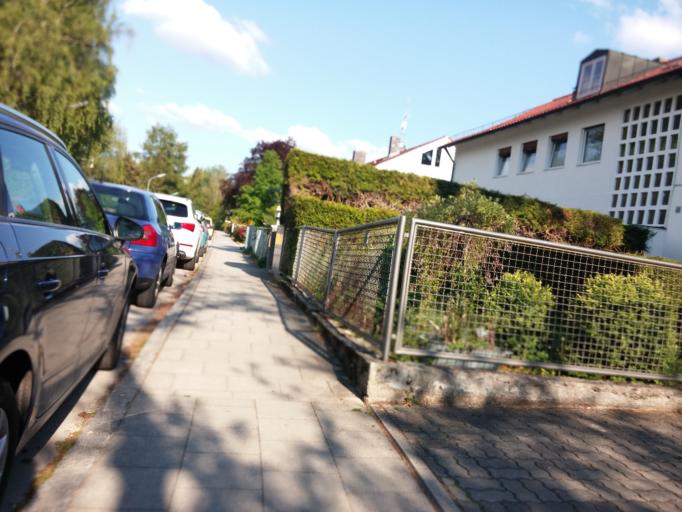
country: DE
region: Bavaria
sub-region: Upper Bavaria
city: Vaterstetten
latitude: 48.0958
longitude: 11.7941
